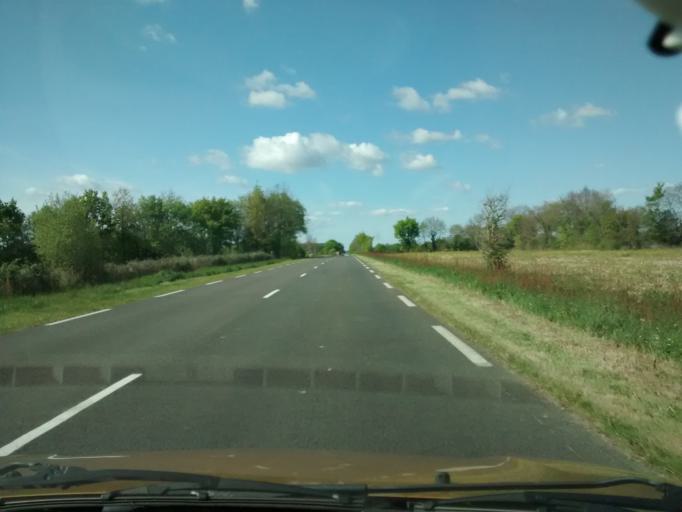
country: FR
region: Pays de la Loire
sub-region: Departement de la Vendee
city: Les Lucs-sur-Boulogne
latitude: 46.8820
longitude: -1.5006
